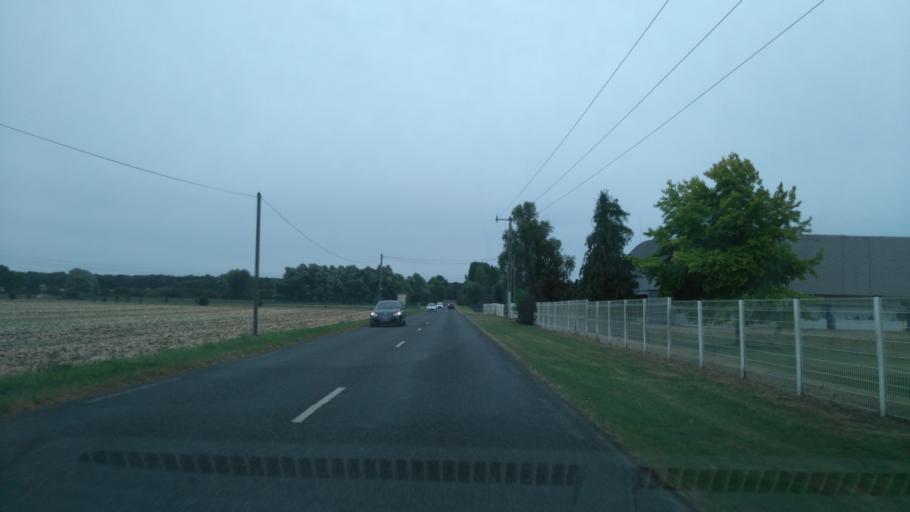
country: FR
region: Picardie
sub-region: Departement de l'Oise
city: Precy-sur-Oise
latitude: 49.1983
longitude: 2.3789
